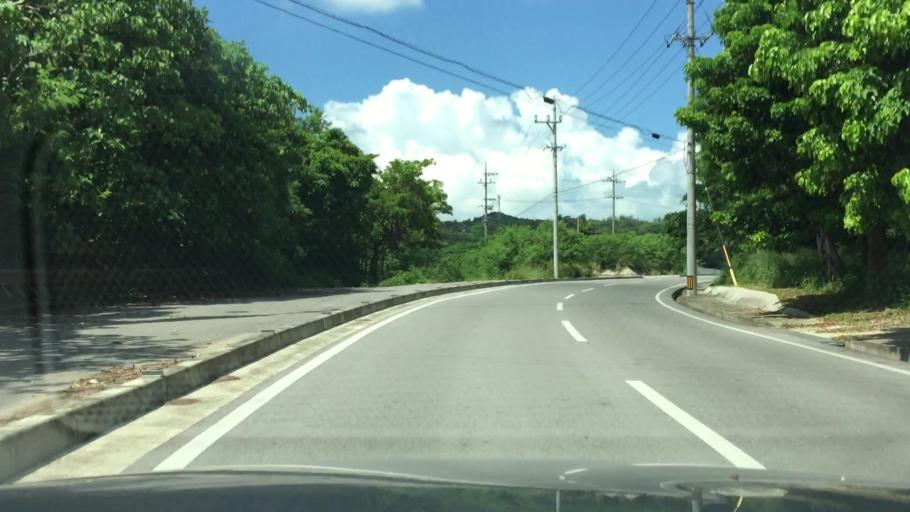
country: JP
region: Okinawa
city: Ishigaki
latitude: 24.3791
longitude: 124.1320
